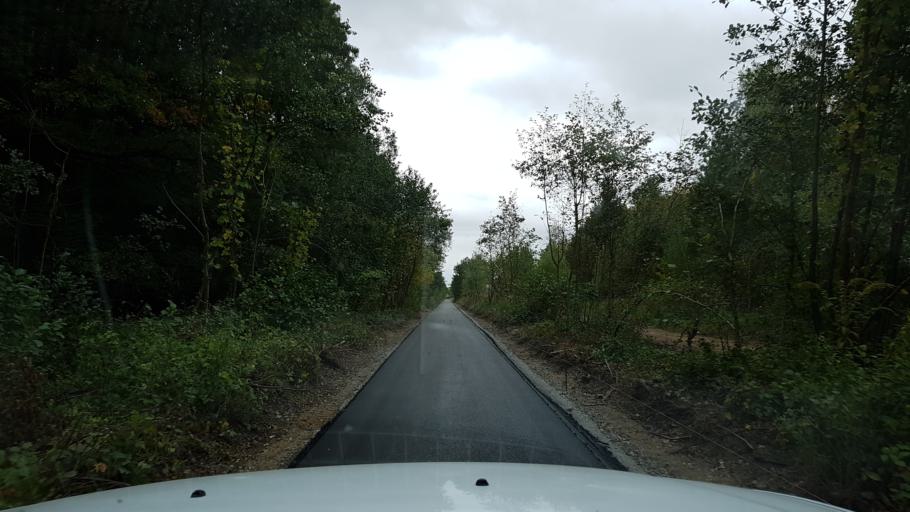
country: PL
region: West Pomeranian Voivodeship
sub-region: Powiat gryfinski
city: Cedynia
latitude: 52.8246
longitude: 14.2382
